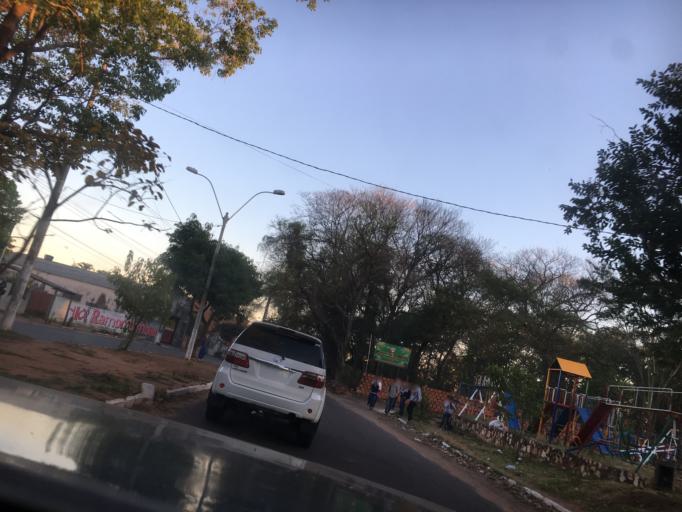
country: PY
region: Central
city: Lambare
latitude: -25.3301
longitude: -57.6093
